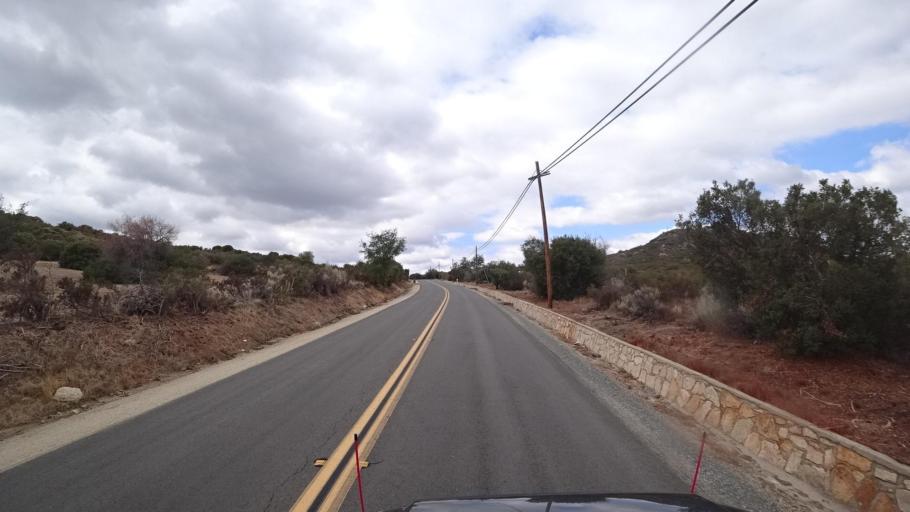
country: US
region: California
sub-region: San Diego County
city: Campo
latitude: 32.6466
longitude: -116.4894
